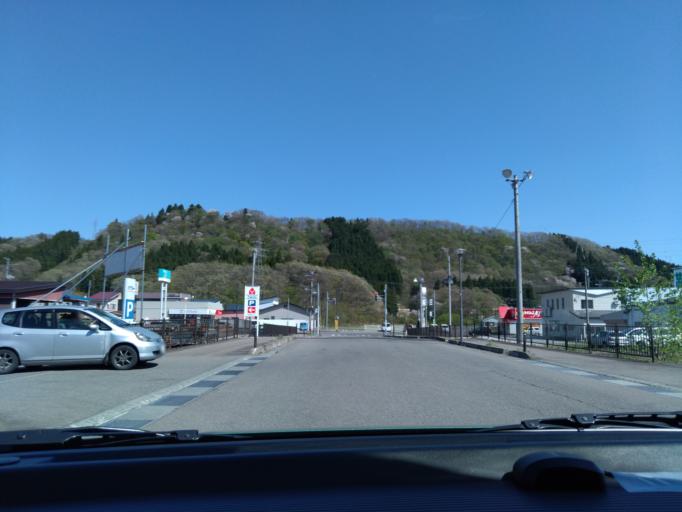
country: JP
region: Akita
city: Kakunodatemachi
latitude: 39.5908
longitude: 140.5731
